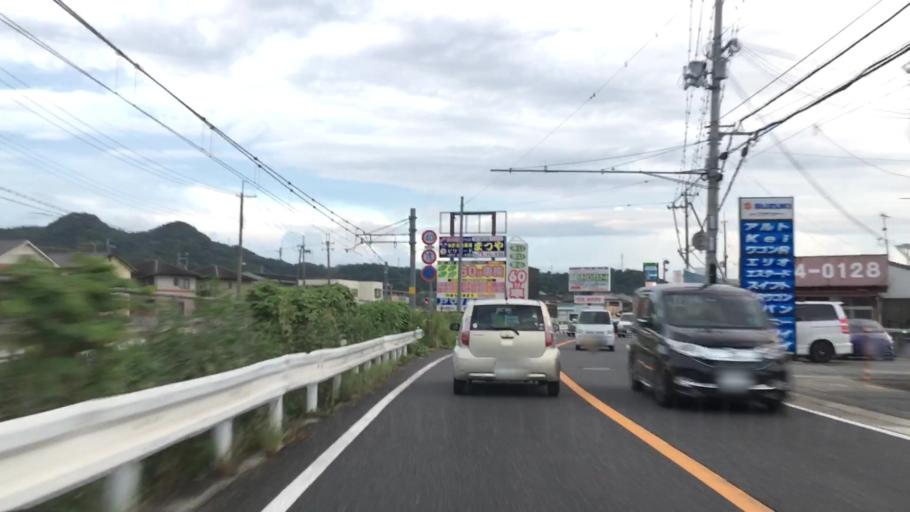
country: JP
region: Hyogo
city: Himeji
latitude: 34.8797
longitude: 134.7288
